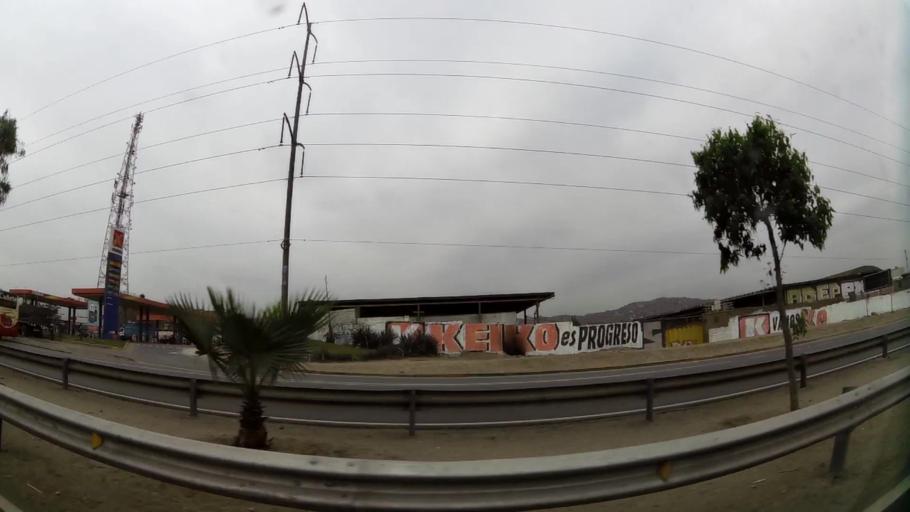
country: PE
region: Lima
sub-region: Lima
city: Surco
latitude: -12.1743
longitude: -76.9781
